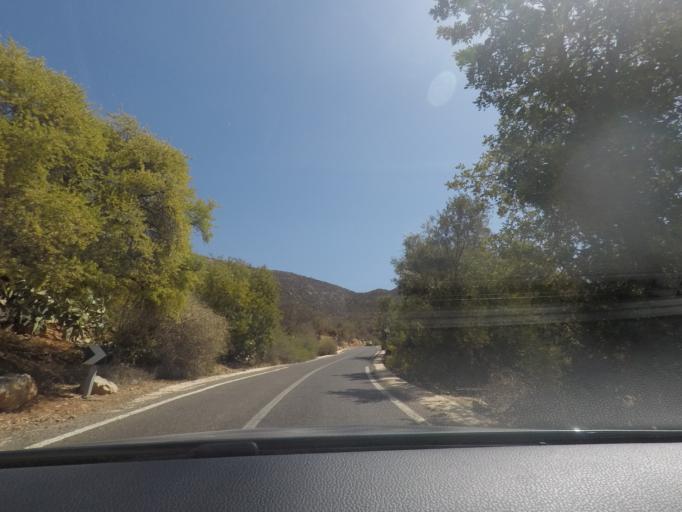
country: MA
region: Souss-Massa-Draa
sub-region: Agadir-Ida-ou-Tnan
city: Aourir
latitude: 30.5982
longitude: -9.5138
